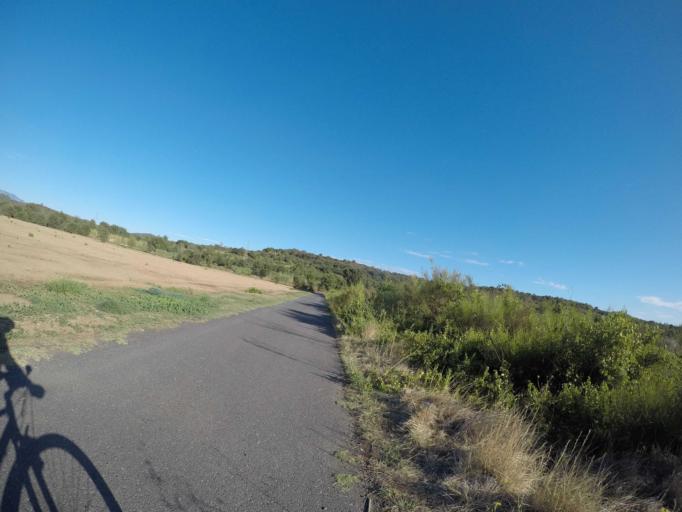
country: FR
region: Languedoc-Roussillon
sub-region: Departement des Pyrenees-Orientales
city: Sant Joan de Pladecorts
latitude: 42.5141
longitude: 2.7777
